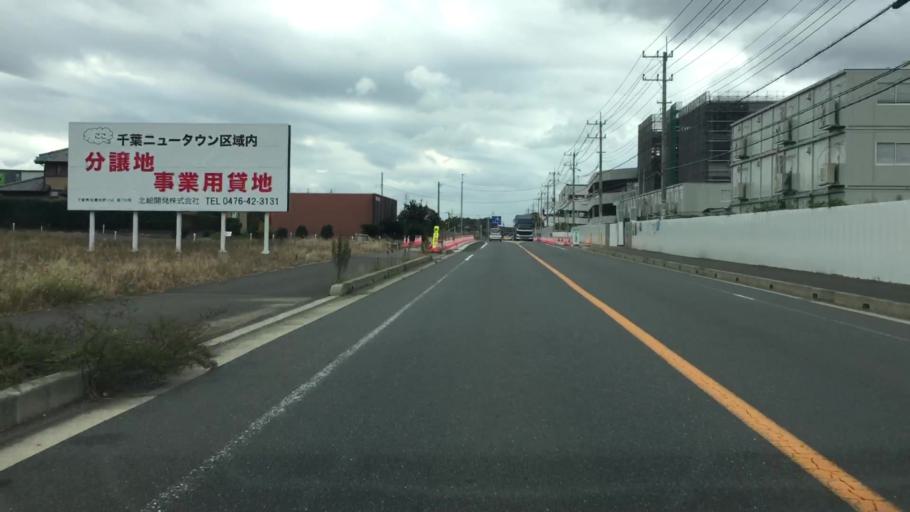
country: JP
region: Chiba
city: Shiroi
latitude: 35.8179
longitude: 140.1354
